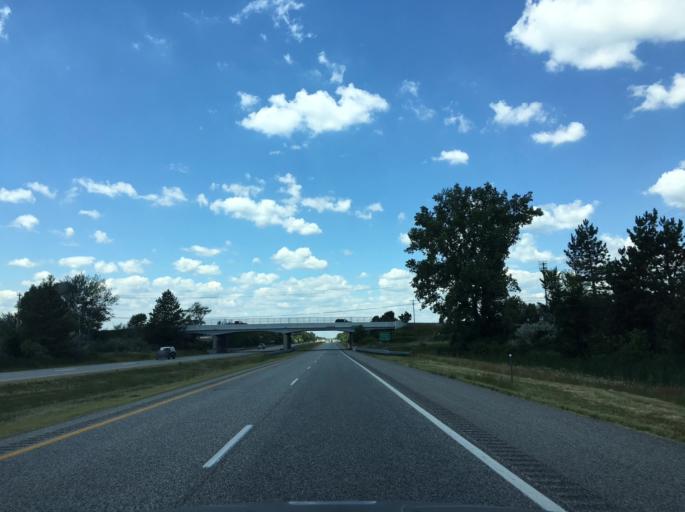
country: US
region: Michigan
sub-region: Midland County
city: Midland
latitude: 43.6560
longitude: -84.2251
